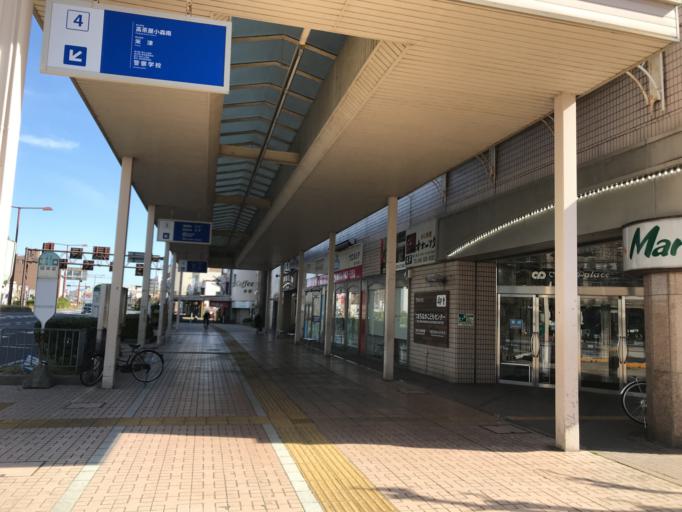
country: JP
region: Mie
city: Tsu-shi
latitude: 34.7186
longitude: 136.5107
